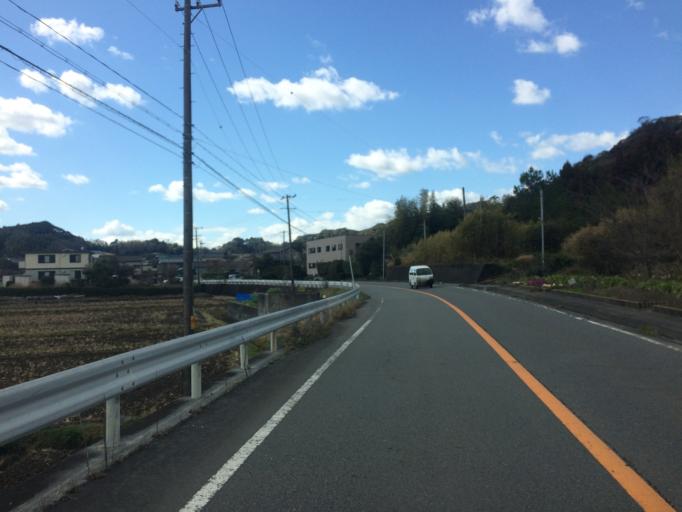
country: JP
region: Shizuoka
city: Shimada
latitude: 34.7760
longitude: 138.2060
